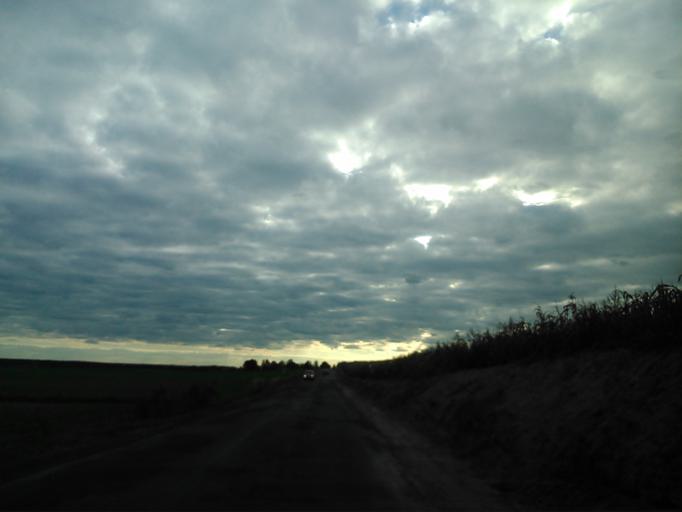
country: PL
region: Kujawsko-Pomorskie
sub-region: Powiat golubsko-dobrzynski
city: Kowalewo Pomorskie
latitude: 53.1341
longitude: 18.9525
